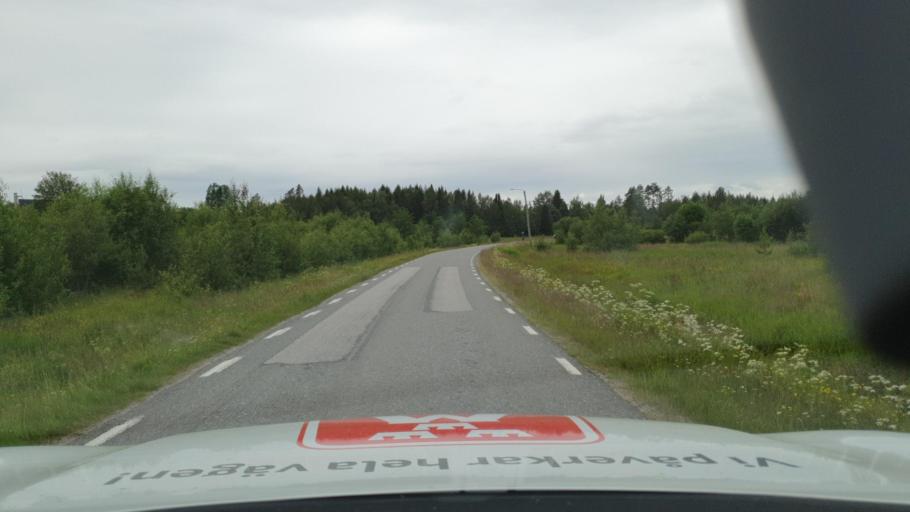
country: SE
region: Vaesterbotten
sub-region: Nordmalings Kommun
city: Nordmaling
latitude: 63.4990
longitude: 19.4224
